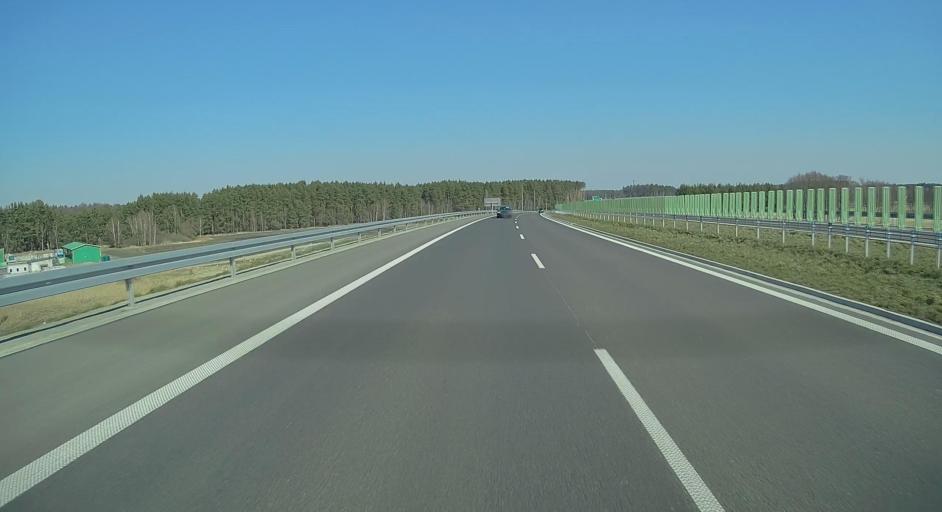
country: PL
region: Subcarpathian Voivodeship
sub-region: Powiat nizanski
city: Konczyce
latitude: 50.4653
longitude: 22.1429
